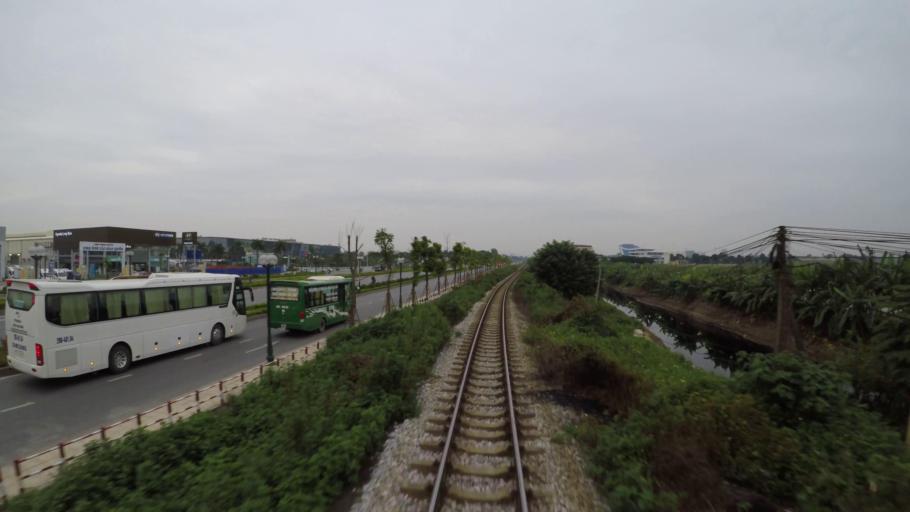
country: VN
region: Ha Noi
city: Trau Quy
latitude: 21.0161
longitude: 105.9451
